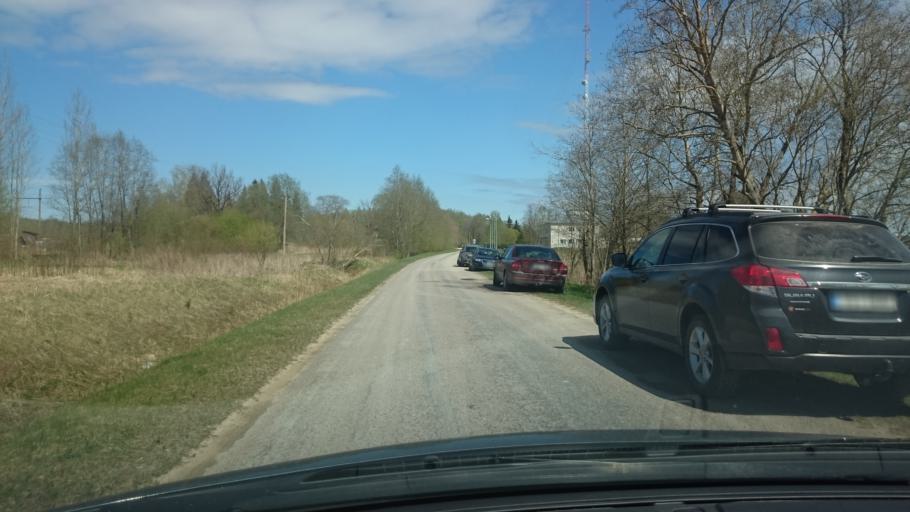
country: EE
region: Ida-Virumaa
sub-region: Sillamaee linn
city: Sillamae
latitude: 59.1388
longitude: 27.8146
